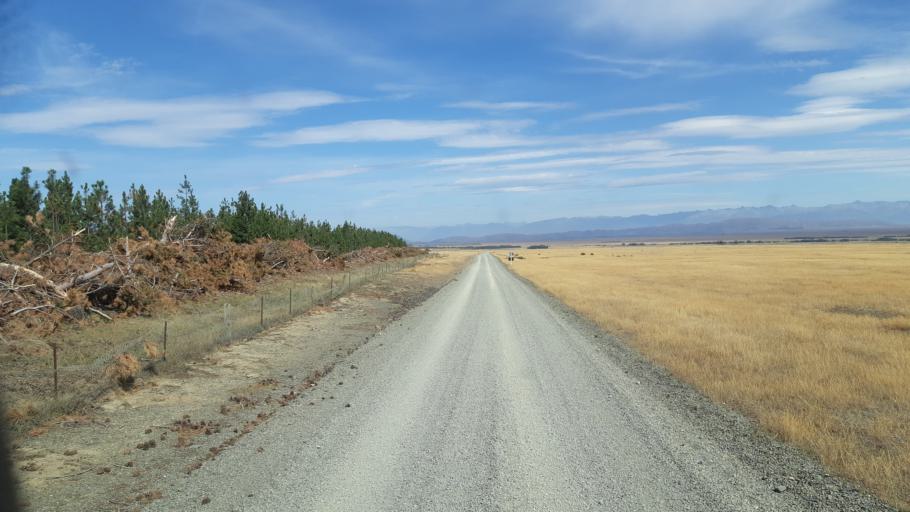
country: NZ
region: Canterbury
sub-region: Timaru District
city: Pleasant Point
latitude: -44.1937
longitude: 170.5665
